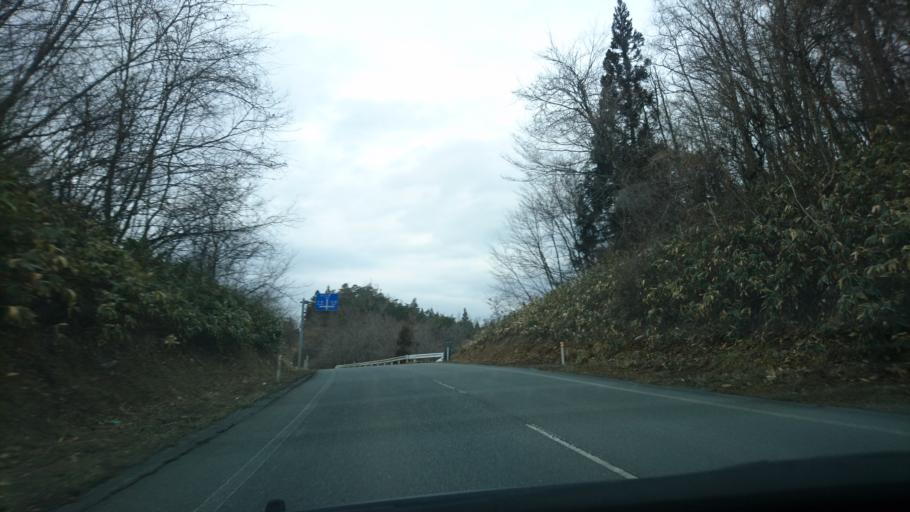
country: JP
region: Iwate
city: Ichinoseki
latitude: 38.9730
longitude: 141.3560
